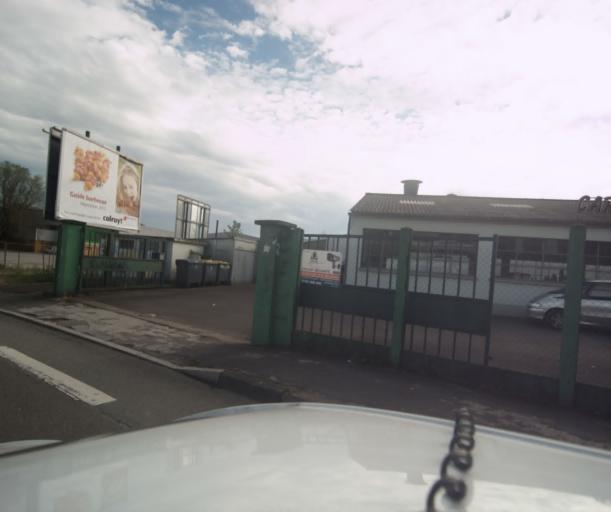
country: FR
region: Franche-Comte
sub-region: Departement du Doubs
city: Pirey
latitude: 47.2406
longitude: 5.9866
